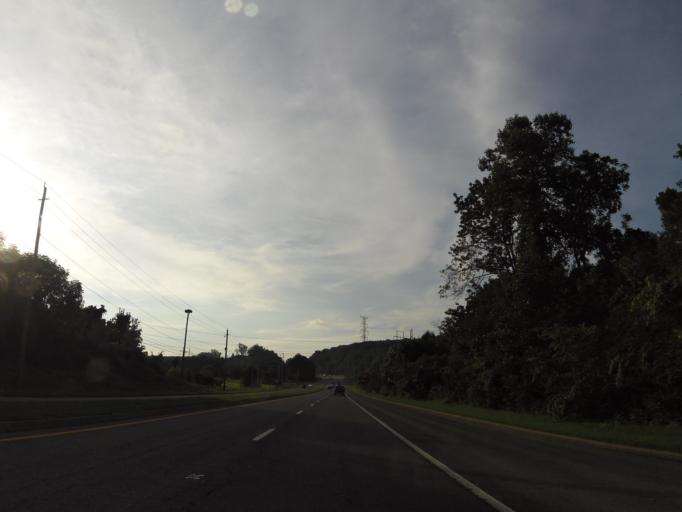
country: US
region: Tennessee
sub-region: Anderson County
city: Oak Ridge
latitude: 35.9967
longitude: -84.2237
